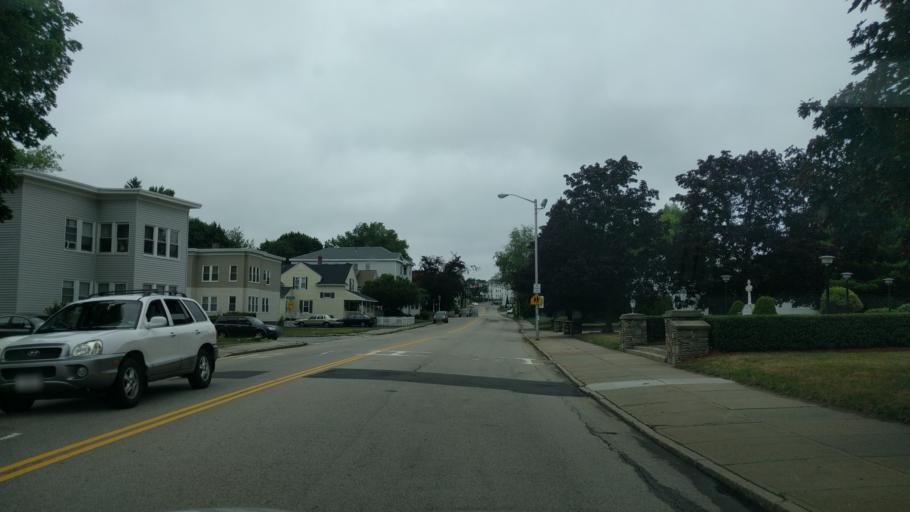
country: US
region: Massachusetts
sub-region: Worcester County
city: Sunderland
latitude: 42.2488
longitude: -71.7781
